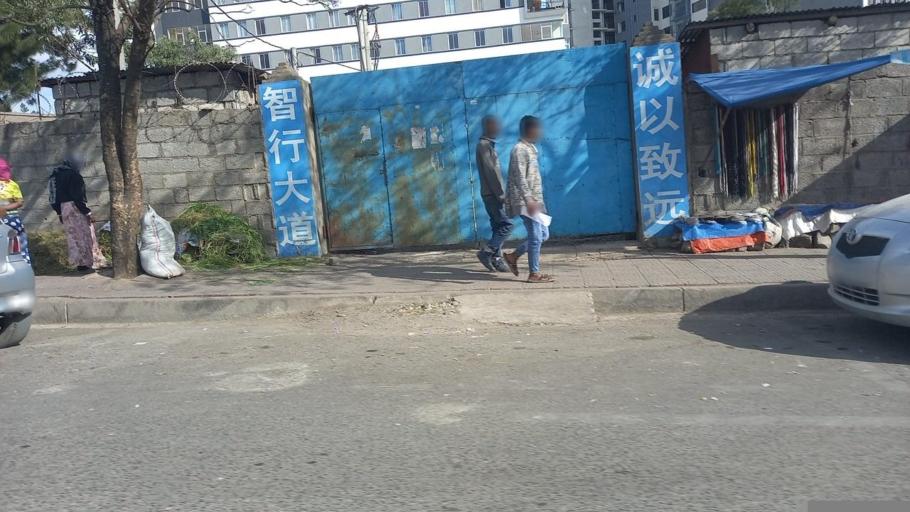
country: ET
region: Adis Abeba
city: Addis Ababa
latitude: 9.0233
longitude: 38.7953
